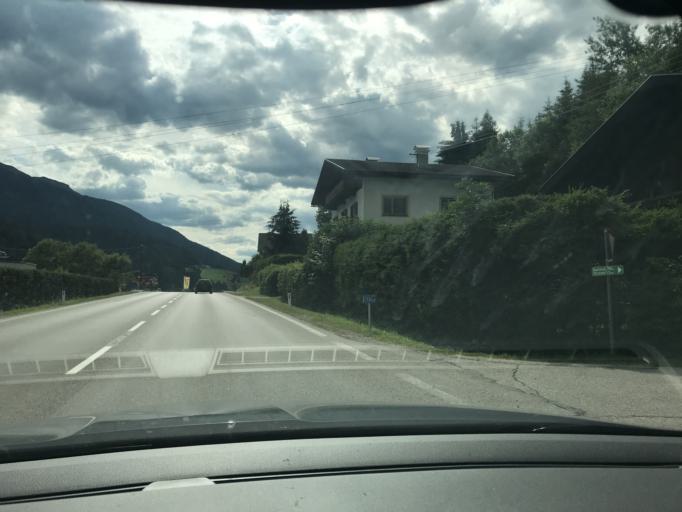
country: AT
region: Tyrol
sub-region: Politischer Bezirk Lienz
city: Strassen
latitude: 46.7494
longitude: 12.4678
